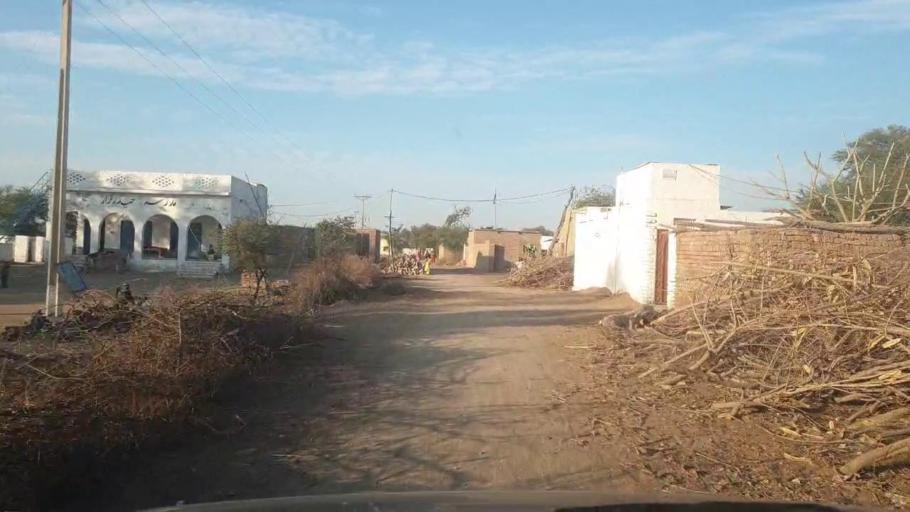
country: PK
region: Sindh
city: Sinjhoro
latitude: 26.0369
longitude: 68.8350
